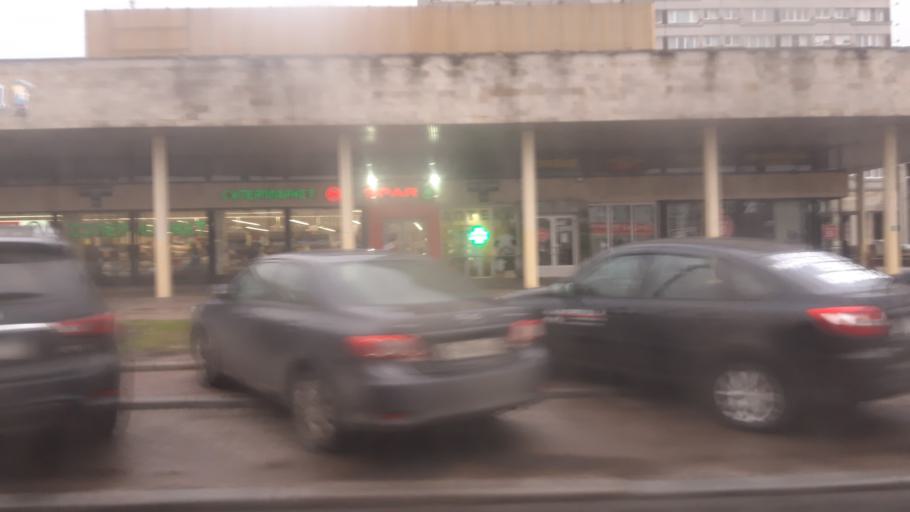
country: RU
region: St.-Petersburg
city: Kupchino
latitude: 59.8449
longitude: 30.3220
